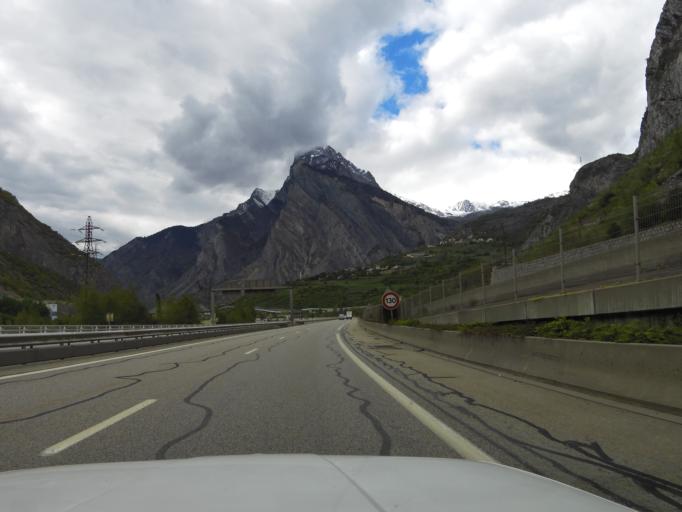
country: FR
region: Rhone-Alpes
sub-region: Departement de la Savoie
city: Saint-Michel-de-Maurienne
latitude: 45.2240
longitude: 6.4504
